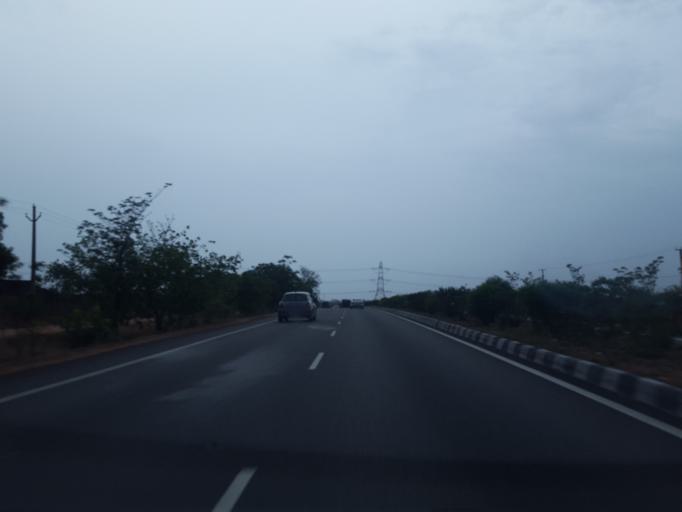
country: IN
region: Telangana
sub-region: Mahbubnagar
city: Farrukhnagar
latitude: 17.0879
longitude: 78.2371
